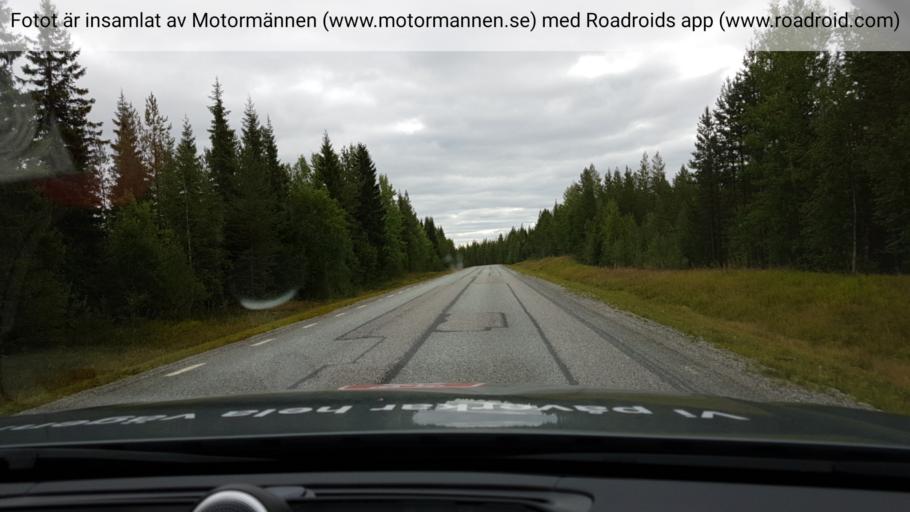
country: SE
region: Jaemtland
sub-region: Stroemsunds Kommun
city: Stroemsund
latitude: 63.8776
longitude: 15.8213
